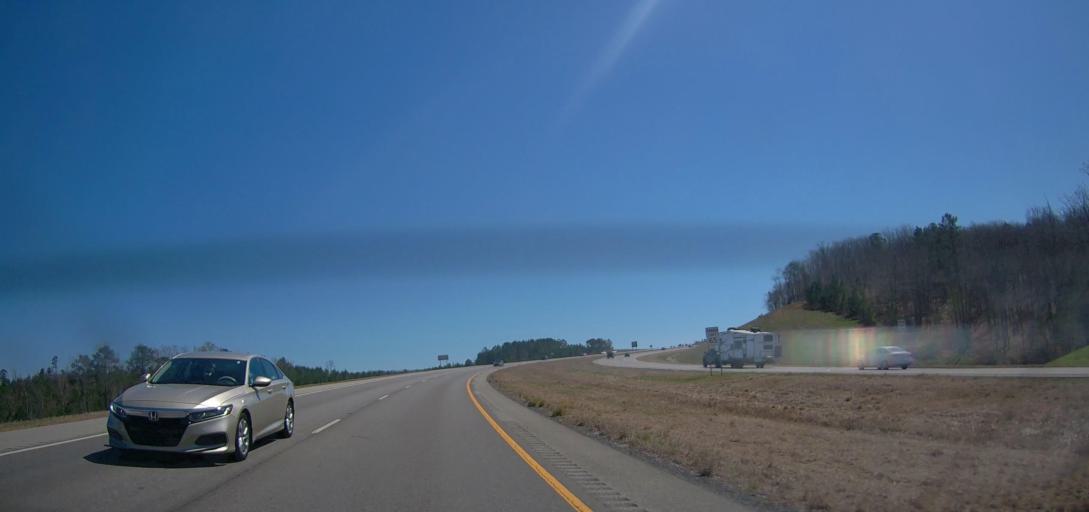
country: US
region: Alabama
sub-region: Calhoun County
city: Saks
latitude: 33.7024
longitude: -85.8139
